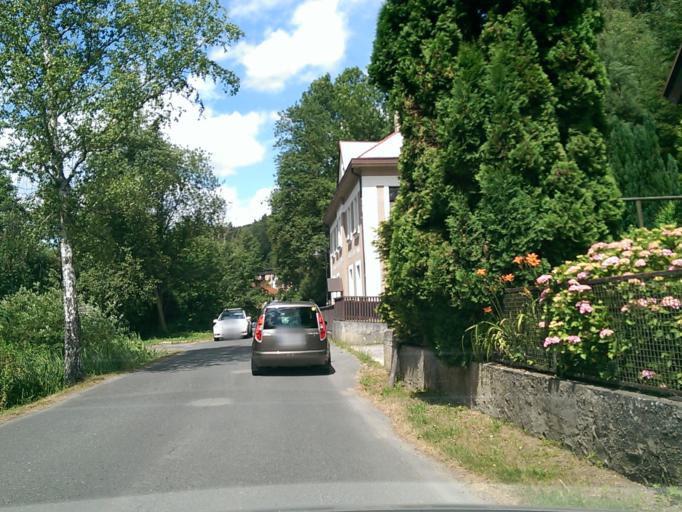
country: CZ
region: Central Bohemia
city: Mseno
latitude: 50.4381
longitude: 14.5807
